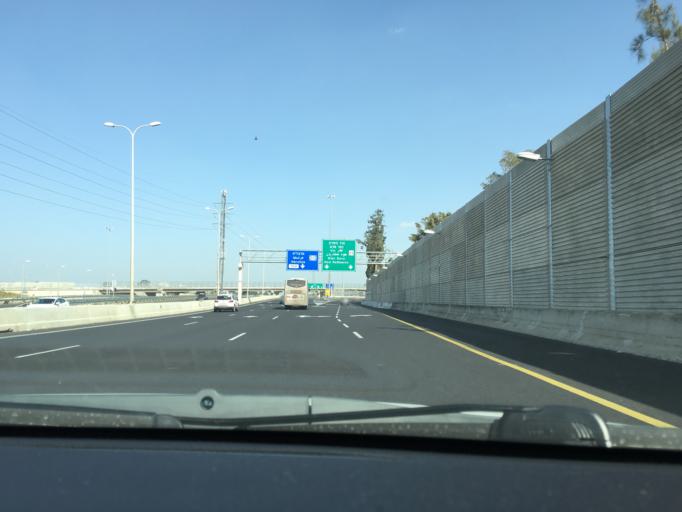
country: IL
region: Central District
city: Hod HaSharon
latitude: 32.1689
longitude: 34.8828
